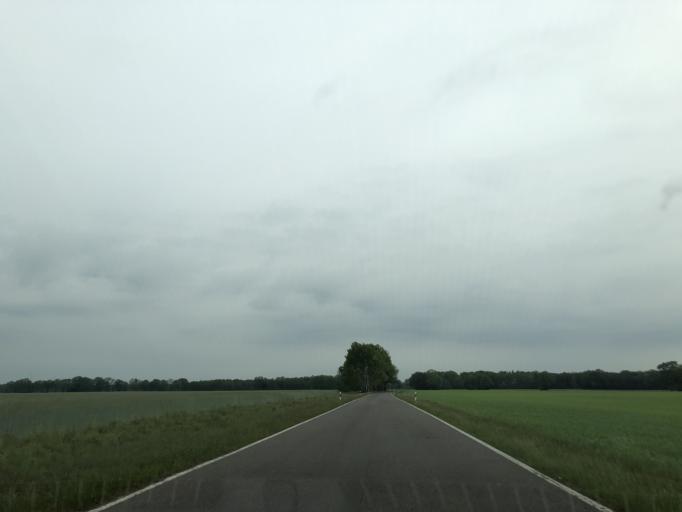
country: DE
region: Brandenburg
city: Plattenburg
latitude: 52.9457
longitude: 12.1163
